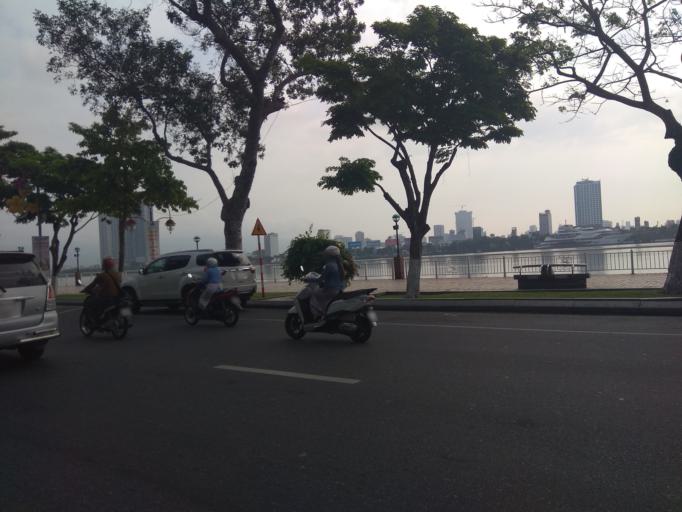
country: VN
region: Da Nang
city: Da Nang
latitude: 16.0632
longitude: 108.2241
